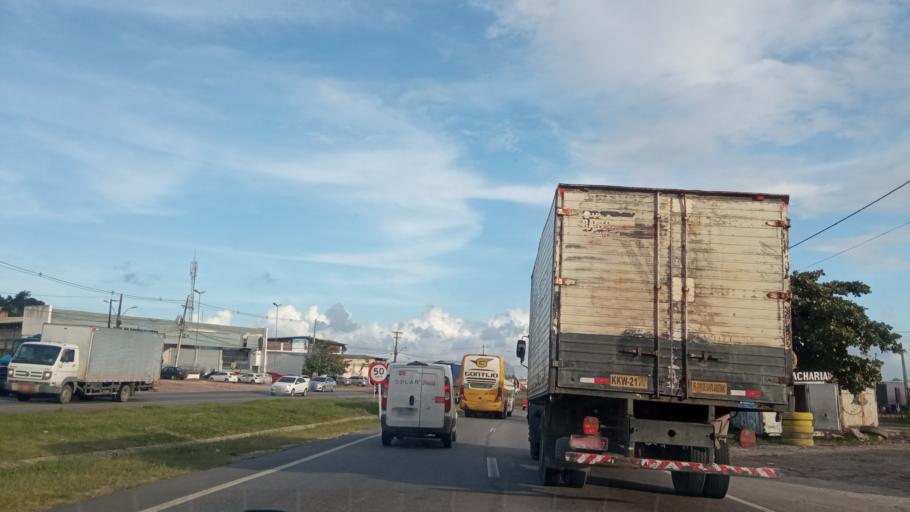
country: BR
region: Pernambuco
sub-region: Jaboatao Dos Guararapes
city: Jaboatao
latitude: -8.1404
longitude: -34.9471
